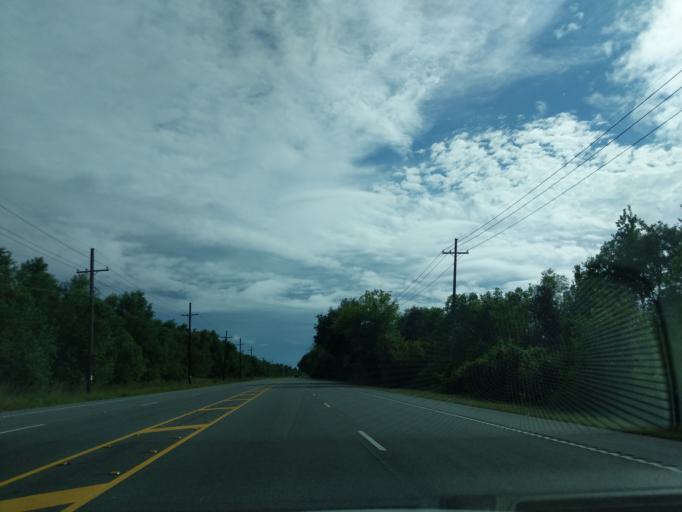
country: US
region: Louisiana
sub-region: Saint Bernard Parish
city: Meraux
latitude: 30.0703
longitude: -89.8641
